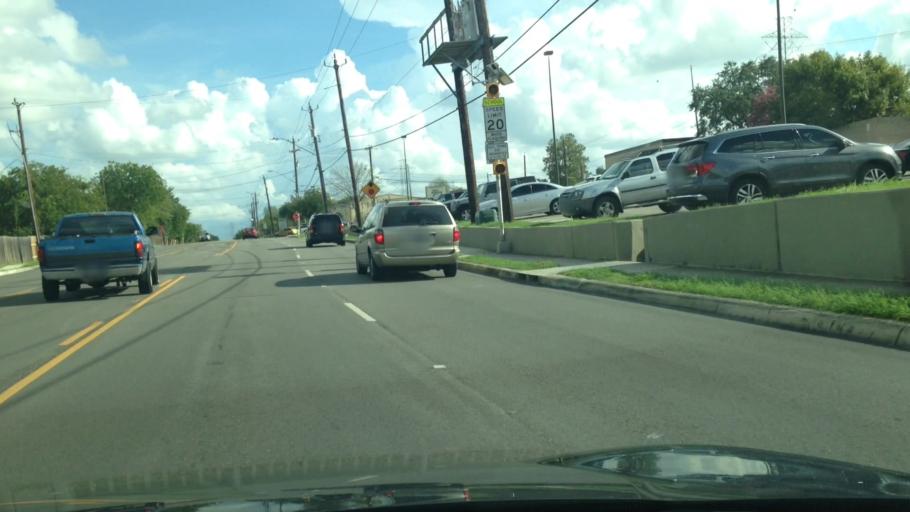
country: US
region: Texas
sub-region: Bexar County
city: Windcrest
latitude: 29.5689
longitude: -98.3950
